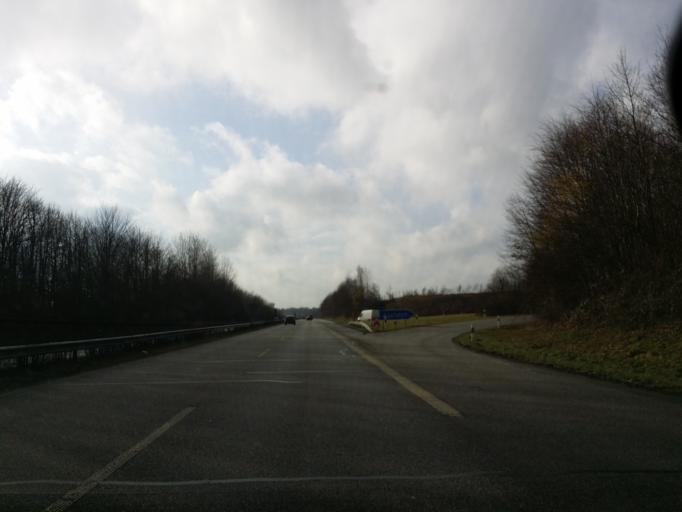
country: DE
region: Schleswig-Holstein
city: Achterwehr
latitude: 54.3193
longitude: 9.9459
